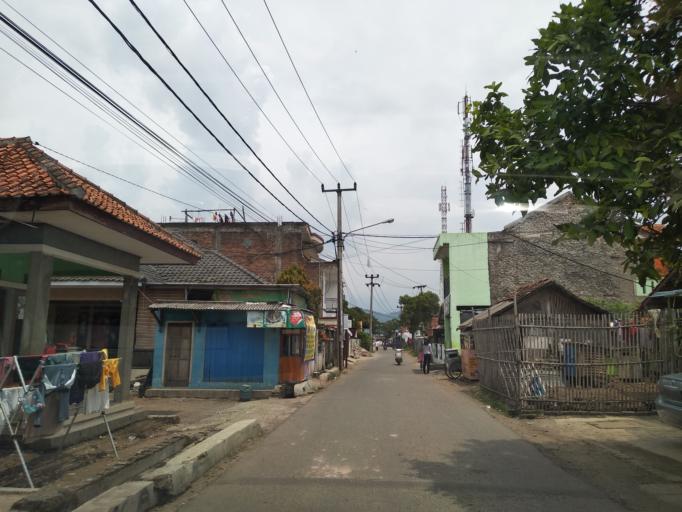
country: ID
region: West Java
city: Pameungpeuk
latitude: -6.9740
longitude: 107.6476
